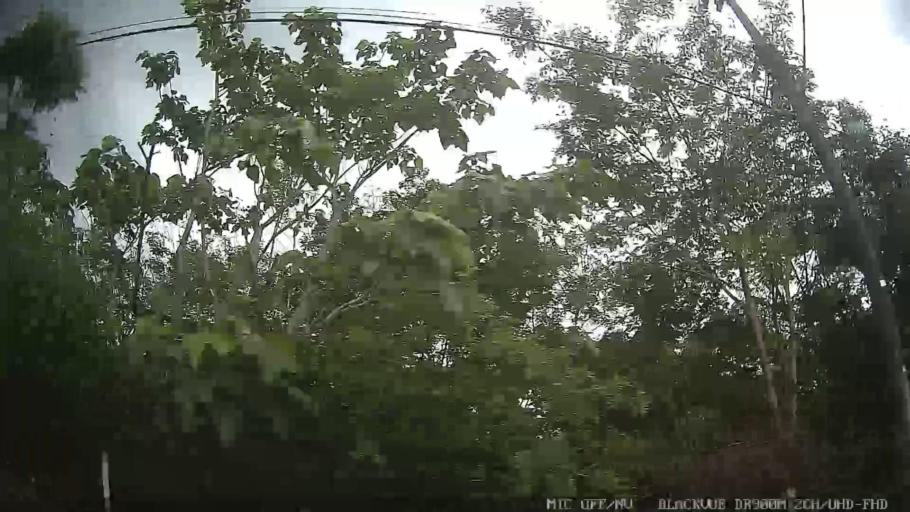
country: BR
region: Sao Paulo
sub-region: Jaguariuna
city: Jaguariuna
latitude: -22.6728
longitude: -46.9733
